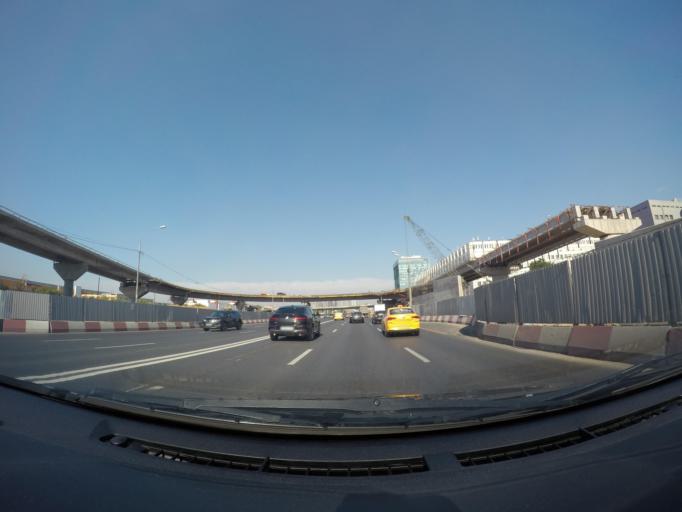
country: RU
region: Moscow
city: Tekstil'shchiki
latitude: 55.7115
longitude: 37.7238
